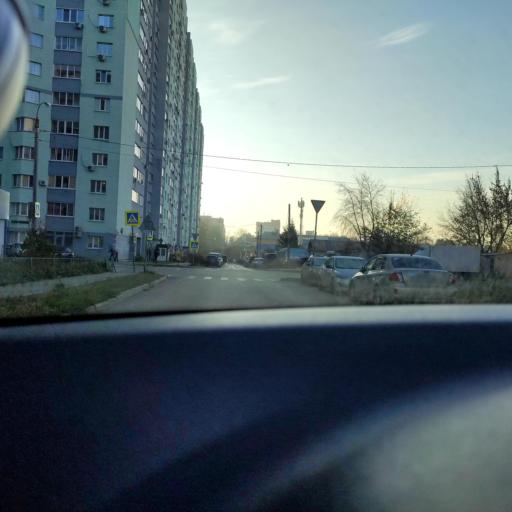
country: RU
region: Samara
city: Samara
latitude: 53.2357
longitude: 50.2548
